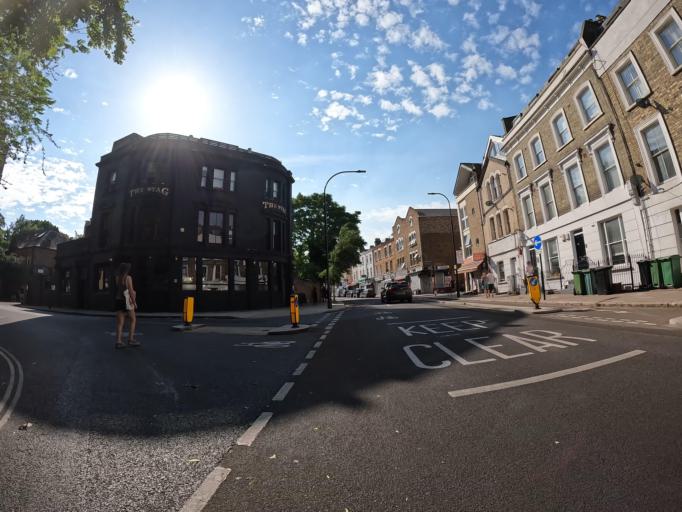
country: GB
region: England
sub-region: Greater London
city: Hendon
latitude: 51.5789
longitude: -0.2015
